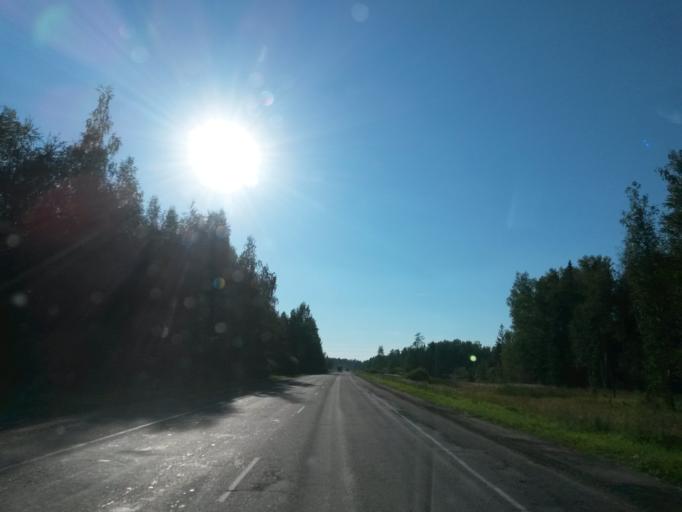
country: RU
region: Ivanovo
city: Novo-Talitsy
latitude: 57.0141
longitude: 40.8059
